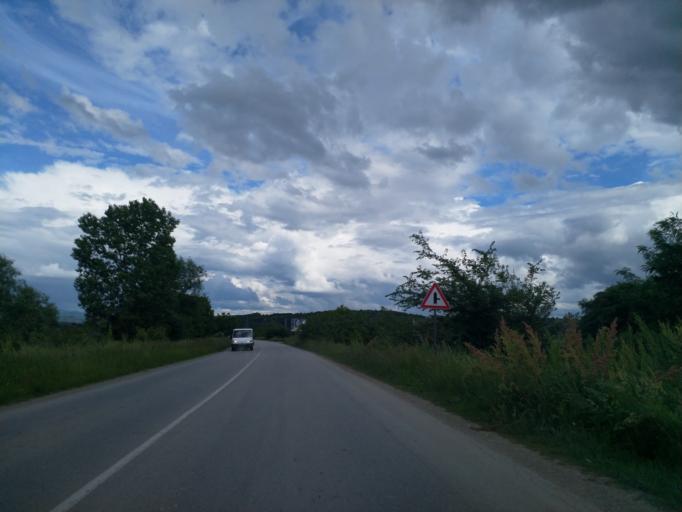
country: RS
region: Central Serbia
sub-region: Pomoravski Okrug
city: Jagodina
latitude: 43.9579
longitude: 21.2897
